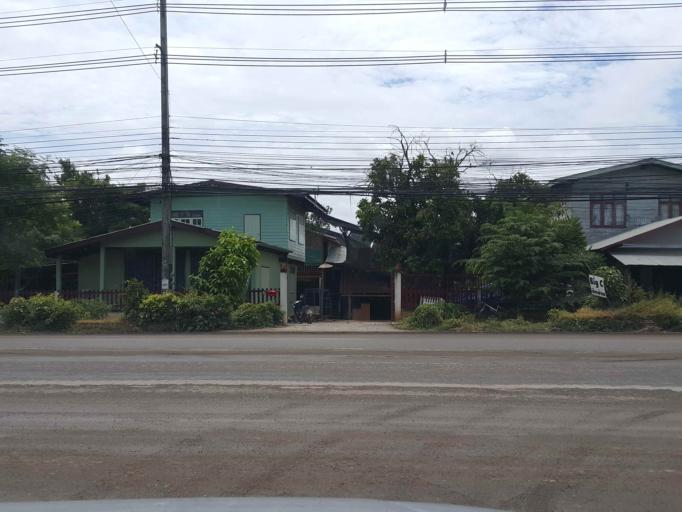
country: TH
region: Sukhothai
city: Ban Na
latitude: 17.0120
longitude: 99.7742
